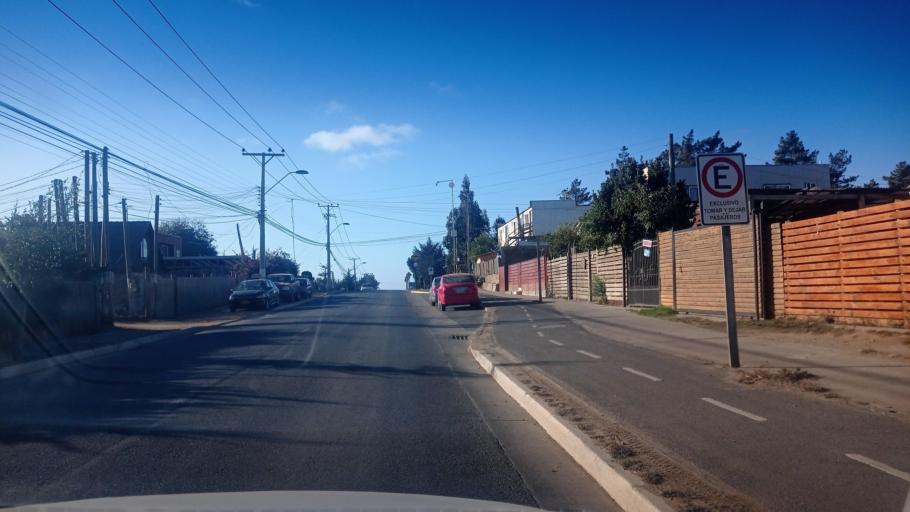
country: CL
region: O'Higgins
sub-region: Provincia de Colchagua
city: Santa Cruz
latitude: -34.4051
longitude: -71.9957
